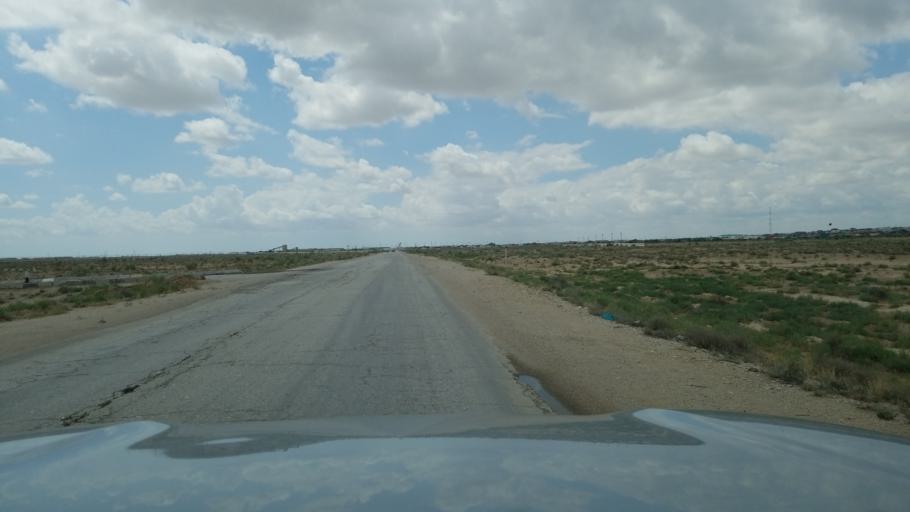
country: TM
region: Balkan
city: Balkanabat
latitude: 39.4883
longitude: 54.4080
